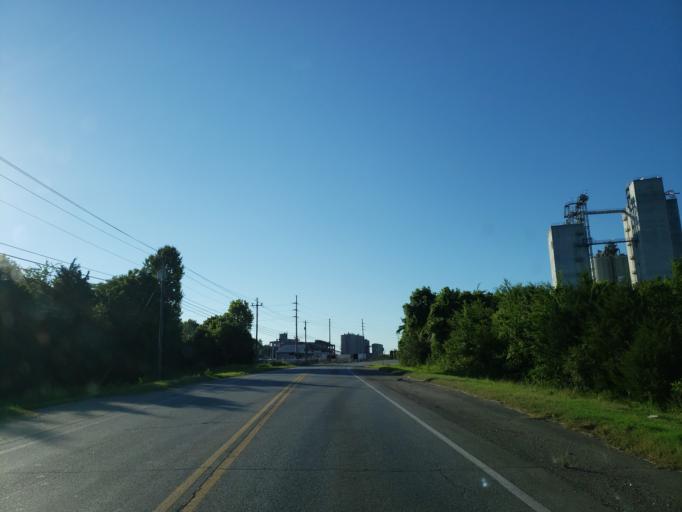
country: US
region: Georgia
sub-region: Polk County
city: Rockmart
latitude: 34.0145
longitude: -85.0470
